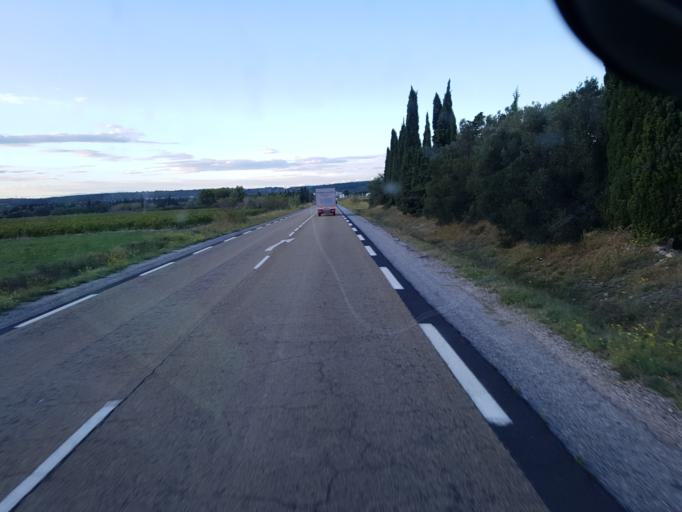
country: FR
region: Languedoc-Roussillon
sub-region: Departement de l'Aude
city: Leucate
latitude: 42.9527
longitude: 2.9864
